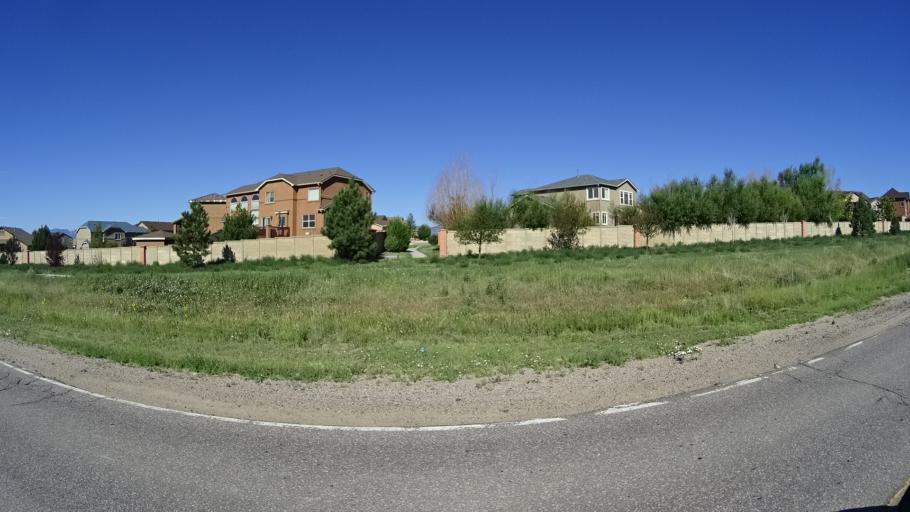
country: US
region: Colorado
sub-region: El Paso County
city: Cimarron Hills
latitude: 38.9206
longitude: -104.6828
